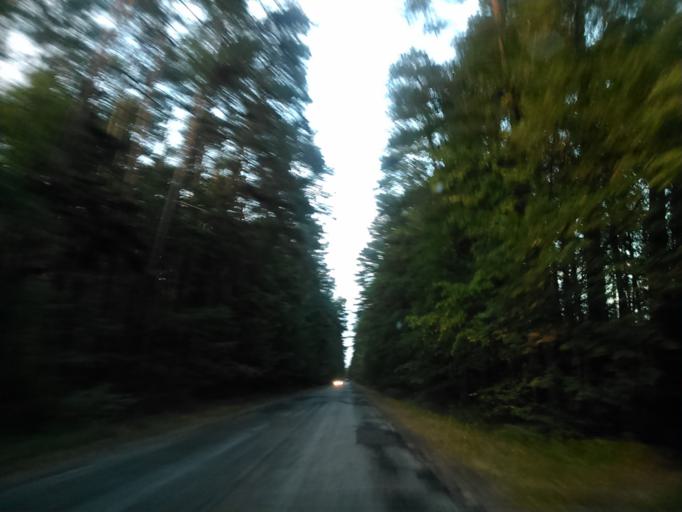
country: PL
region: Kujawsko-Pomorskie
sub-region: Powiat wabrzeski
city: Debowa Laka
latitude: 53.1807
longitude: 19.1449
